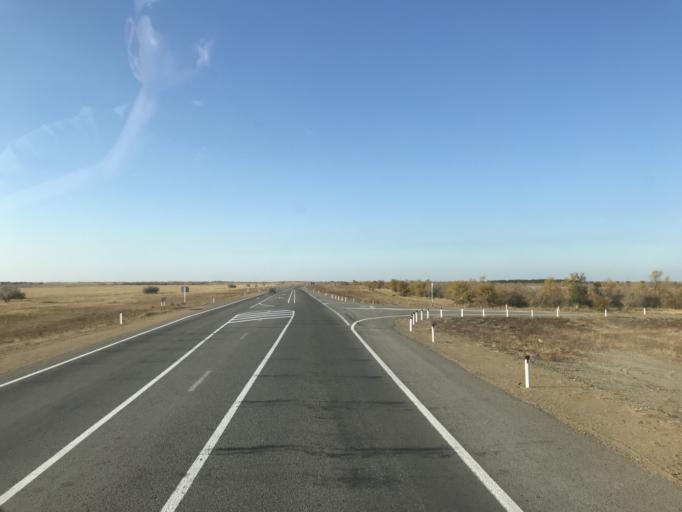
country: KZ
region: Pavlodar
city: Koktobe
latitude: 51.8000
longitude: 77.4823
